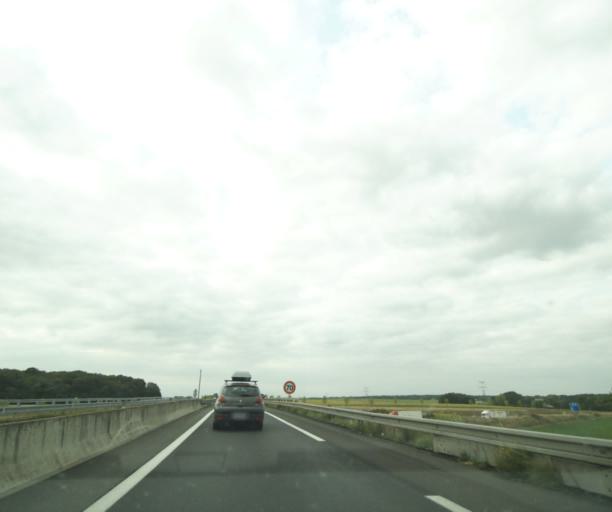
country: FR
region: Centre
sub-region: Departement d'Indre-et-Loire
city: Parcay-Meslay
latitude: 47.4645
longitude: 0.7644
